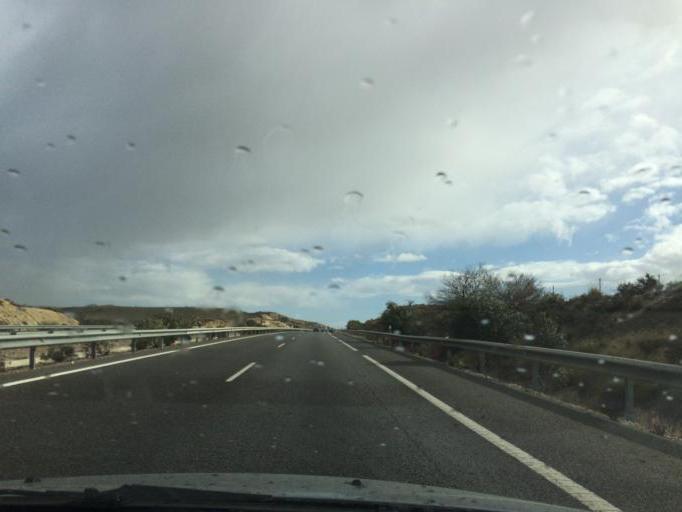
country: ES
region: Andalusia
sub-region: Provincia de Almeria
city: Retamar
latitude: 36.8714
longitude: -2.2917
